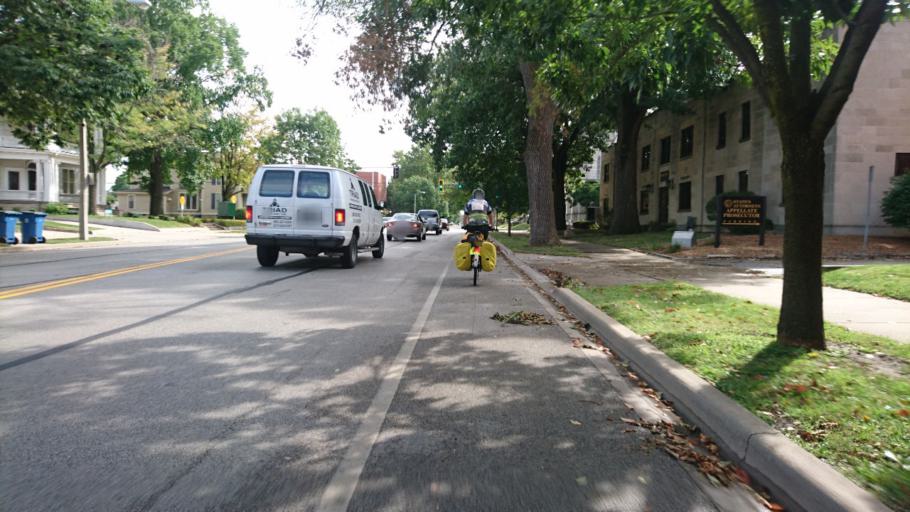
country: US
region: Illinois
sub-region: Sangamon County
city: Springfield
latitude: 39.7946
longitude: -89.6535
